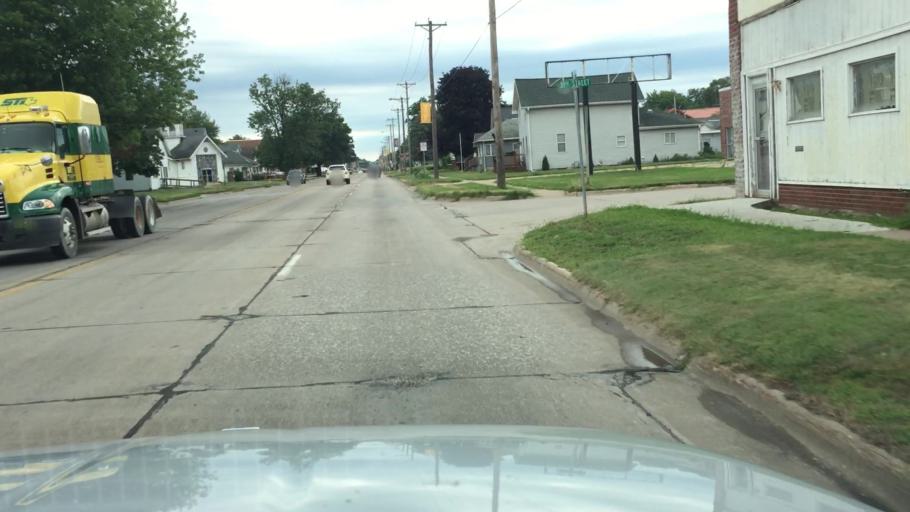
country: US
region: Iowa
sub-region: Lee County
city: Fort Madison
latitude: 40.6267
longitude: -91.3513
